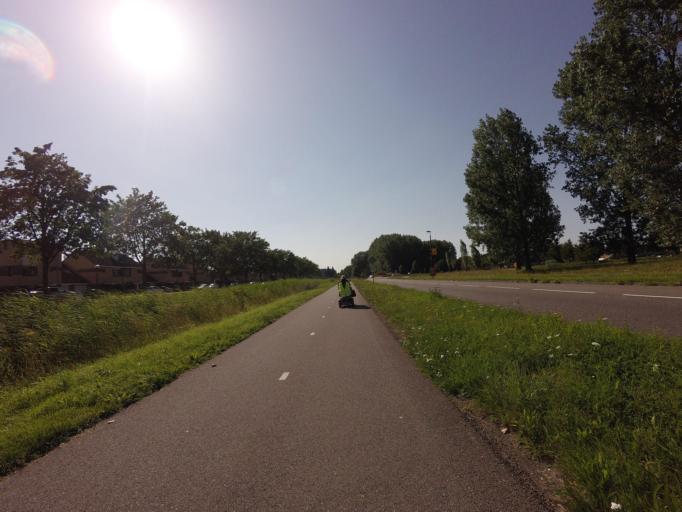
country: NL
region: Utrecht
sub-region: Gemeente Nieuwegein
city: Nieuwegein
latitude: 52.0477
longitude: 5.0821
